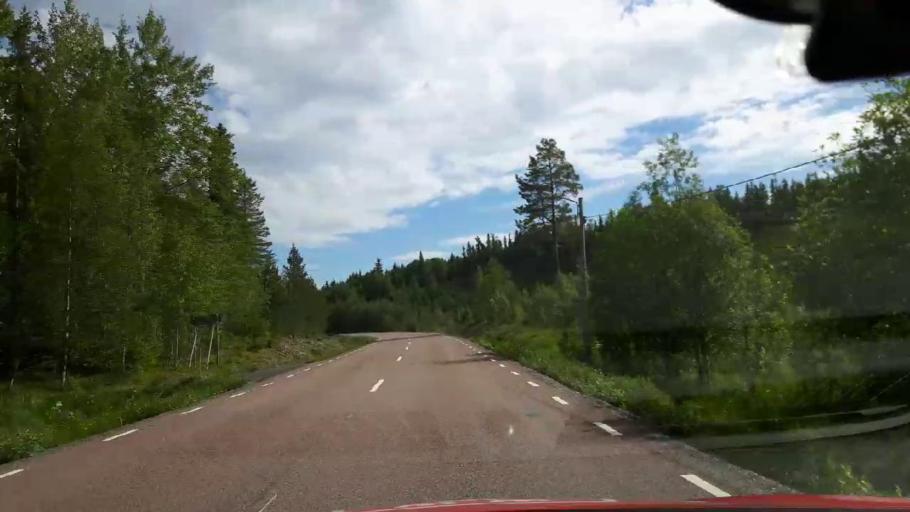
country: SE
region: Jaemtland
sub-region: Krokoms Kommun
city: Valla
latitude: 63.9288
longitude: 14.2109
